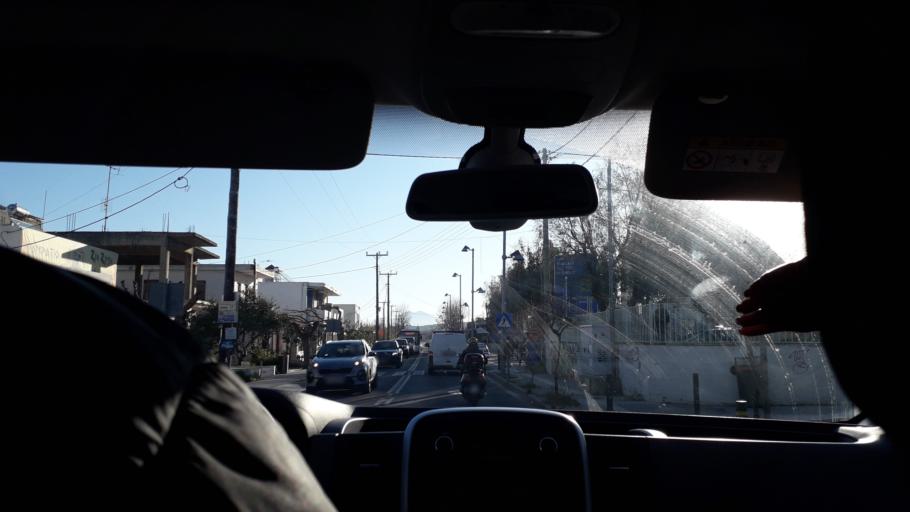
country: GR
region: Crete
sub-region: Nomos Rethymnis
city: Rethymno
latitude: 35.3660
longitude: 24.5111
